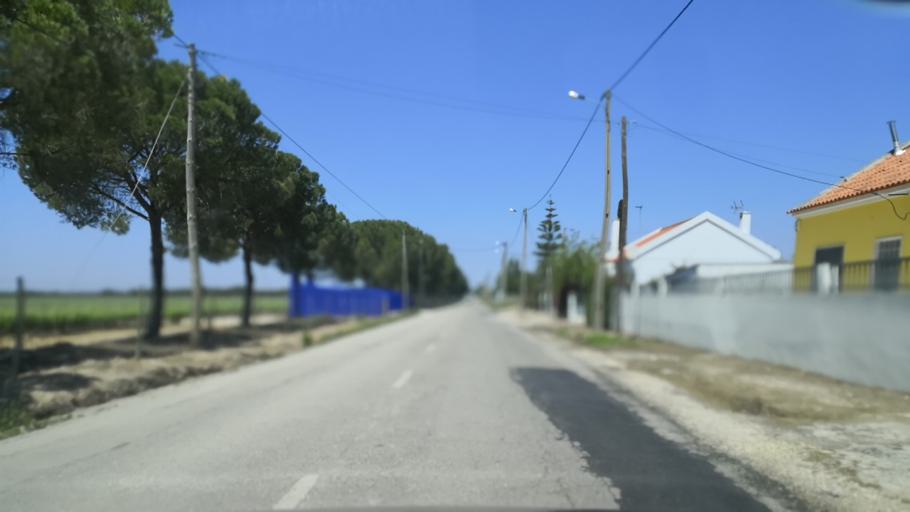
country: PT
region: Santarem
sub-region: Benavente
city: Poceirao
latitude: 38.6810
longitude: -8.7326
